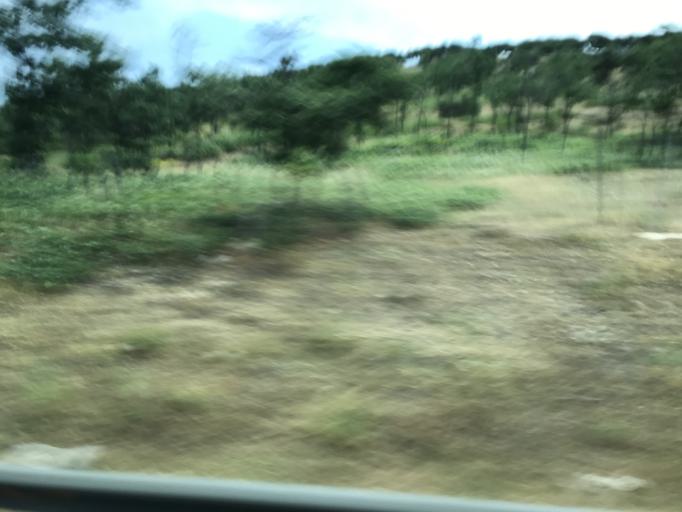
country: ES
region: Madrid
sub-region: Provincia de Madrid
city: Buitrago del Lozoya
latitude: 40.9570
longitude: -3.6413
